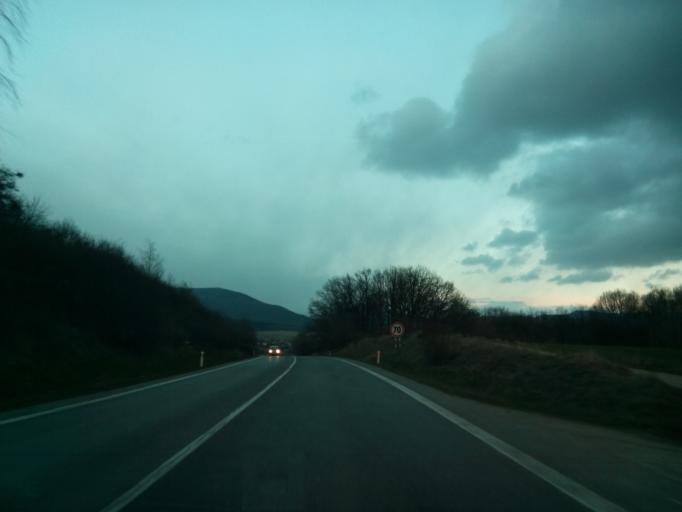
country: SK
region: Kosicky
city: Roznava
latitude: 48.6511
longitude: 20.5801
